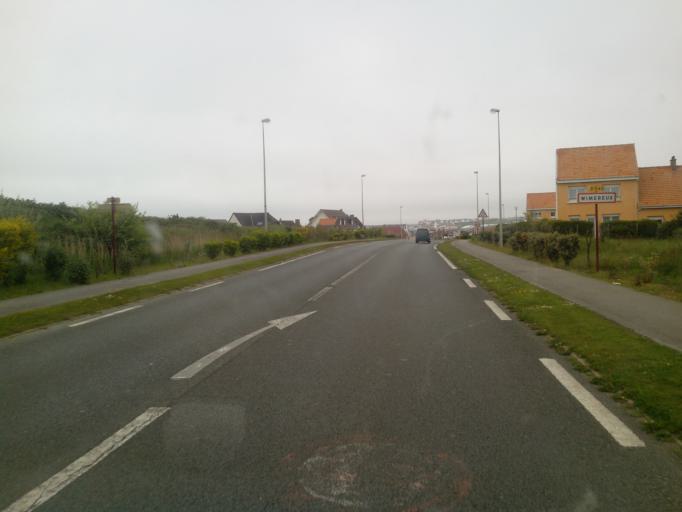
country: FR
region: Nord-Pas-de-Calais
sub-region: Departement du Pas-de-Calais
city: Wimereux
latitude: 50.7598
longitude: 1.6062
